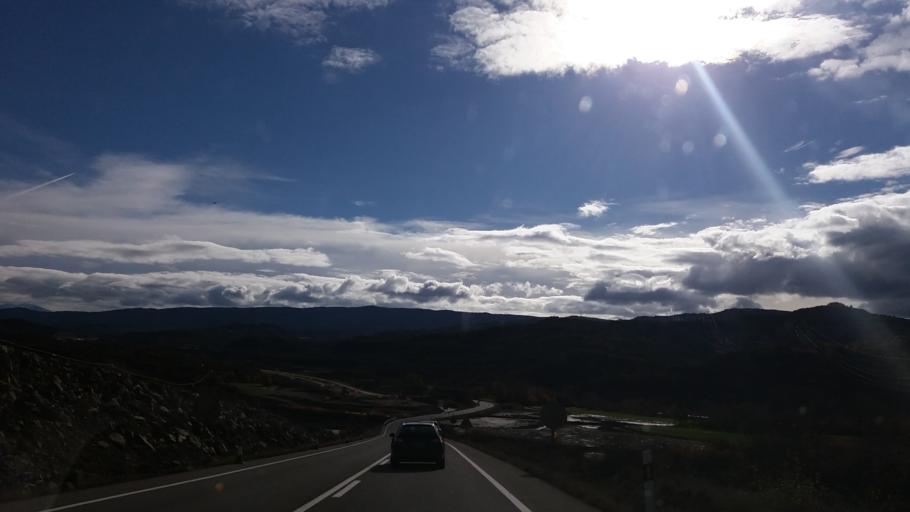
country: ES
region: Aragon
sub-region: Provincia de Huesca
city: Sabinanigo
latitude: 42.4169
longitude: -0.3942
